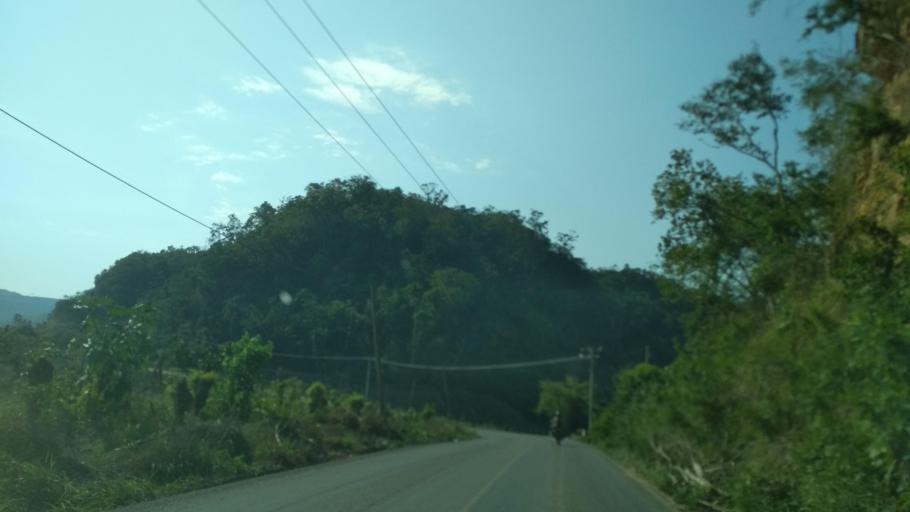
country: MX
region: Veracruz
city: Agua Dulce
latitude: 20.4006
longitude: -97.2471
